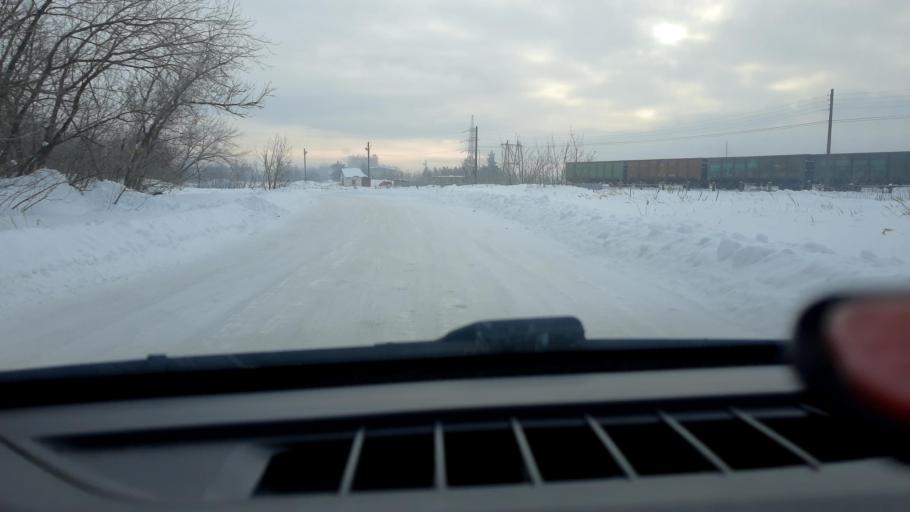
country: RU
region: Nizjnij Novgorod
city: Babino
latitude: 56.2624
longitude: 43.6083
